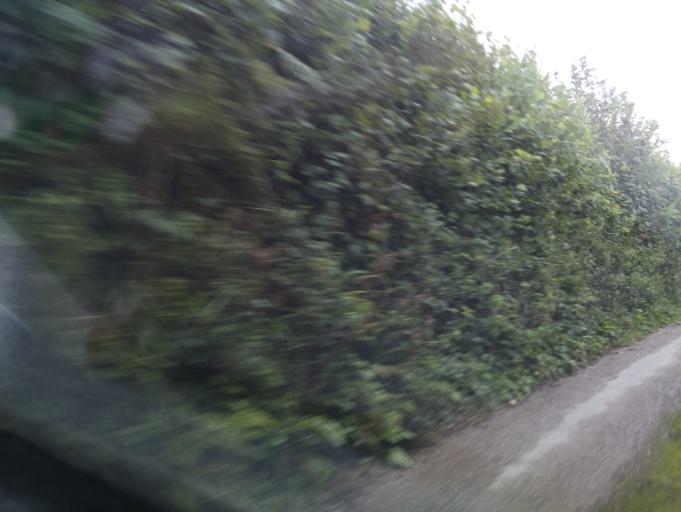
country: GB
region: England
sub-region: Devon
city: Kingsbridge
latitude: 50.2751
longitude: -3.8237
